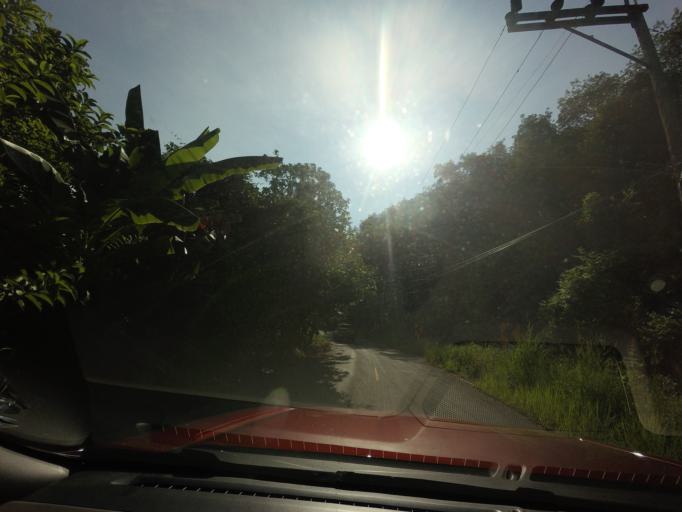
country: TH
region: Yala
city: Than To
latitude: 6.0815
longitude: 101.3308
